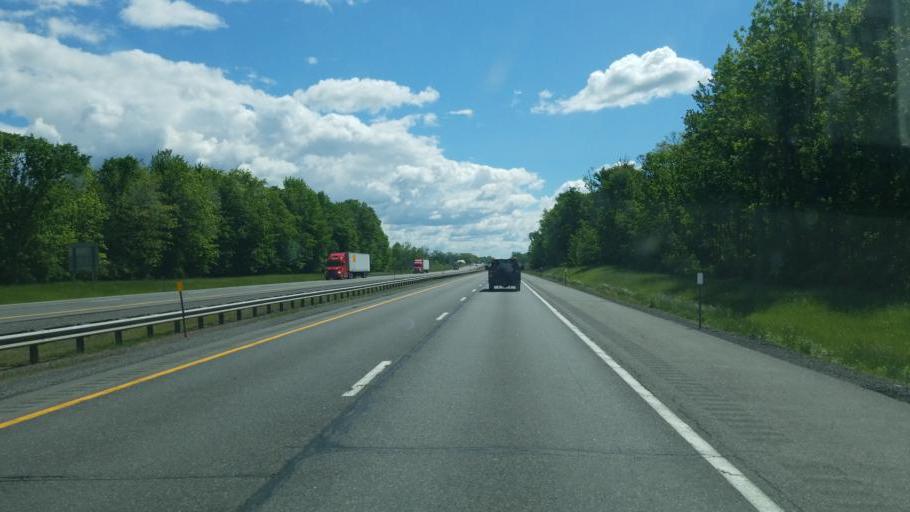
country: US
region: New York
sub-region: Oneida County
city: Vernon
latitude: 43.1265
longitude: -75.5602
